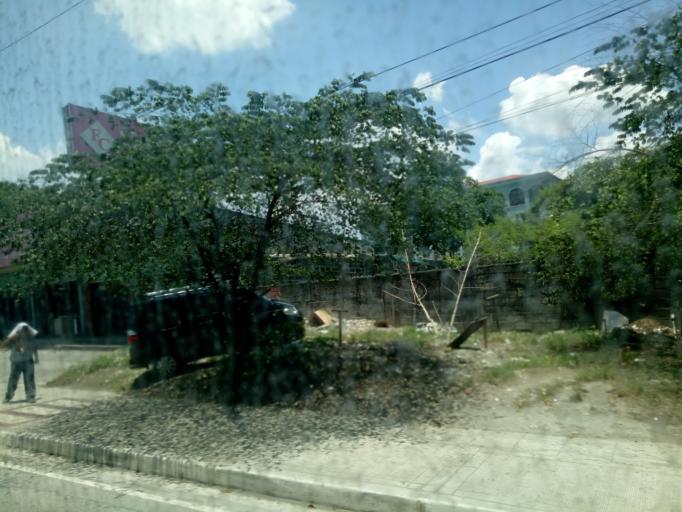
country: PH
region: Calabarzon
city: Bagong Pagasa
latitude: 14.7333
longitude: 121.0511
